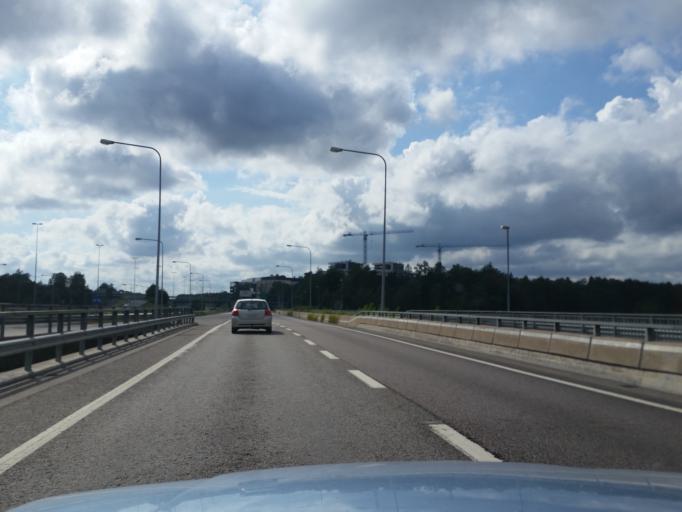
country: FI
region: Uusimaa
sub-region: Helsinki
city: Otaniemi
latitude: 60.1699
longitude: 24.8200
